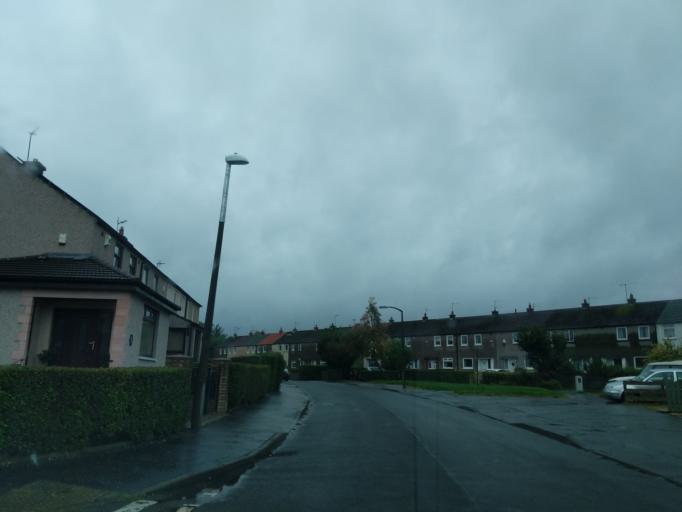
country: GB
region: Scotland
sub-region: Edinburgh
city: Colinton
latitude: 55.9350
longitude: -3.2880
